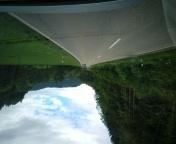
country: DE
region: Baden-Wuerttemberg
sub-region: Freiburg Region
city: Oppenau
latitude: 48.4449
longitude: 8.1698
